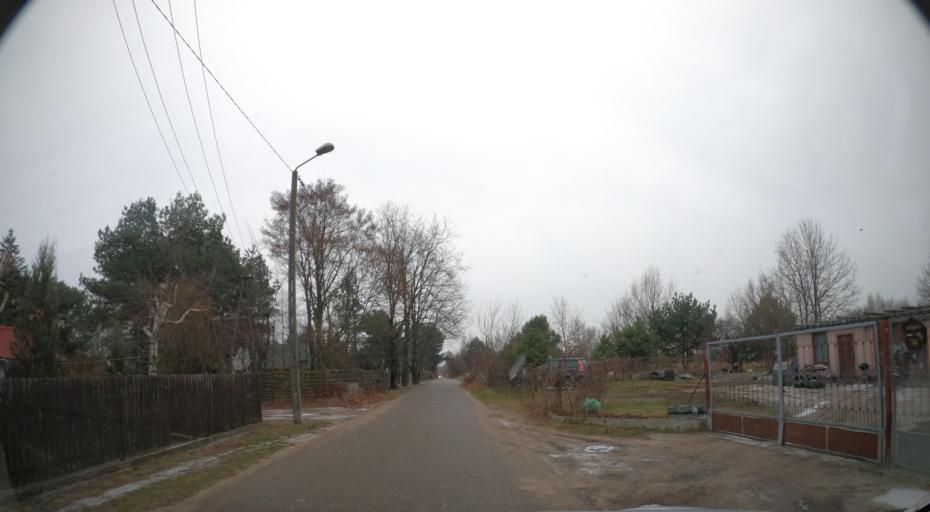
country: PL
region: Masovian Voivodeship
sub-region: Powiat radomski
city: Jastrzebia
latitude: 51.4330
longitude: 21.2288
